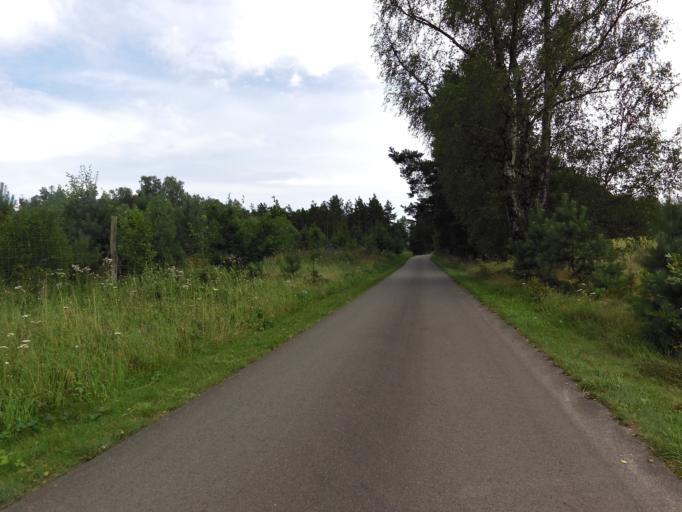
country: DE
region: Brandenburg
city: Lychen
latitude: 53.2654
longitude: 13.3049
